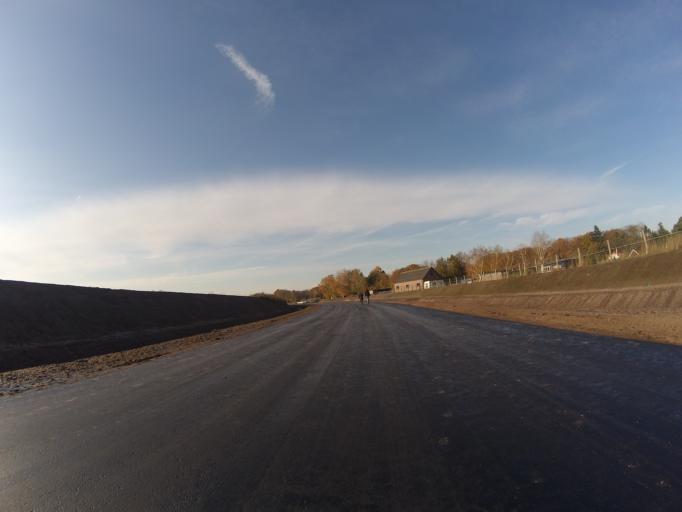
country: NL
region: Gelderland
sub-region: Gemeente Barneveld
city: Voorthuizen
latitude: 52.1928
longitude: 5.6147
